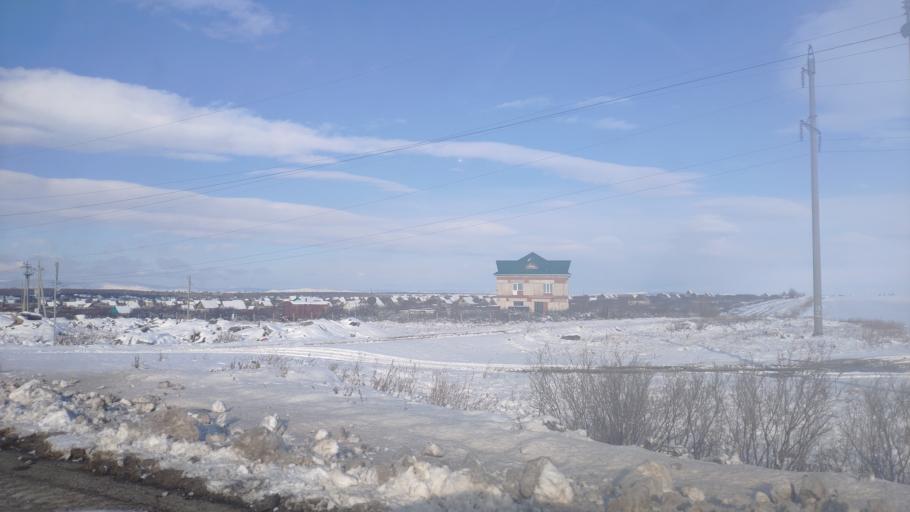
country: RU
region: Bashkortostan
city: Sibay
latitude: 52.7386
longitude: 58.7614
